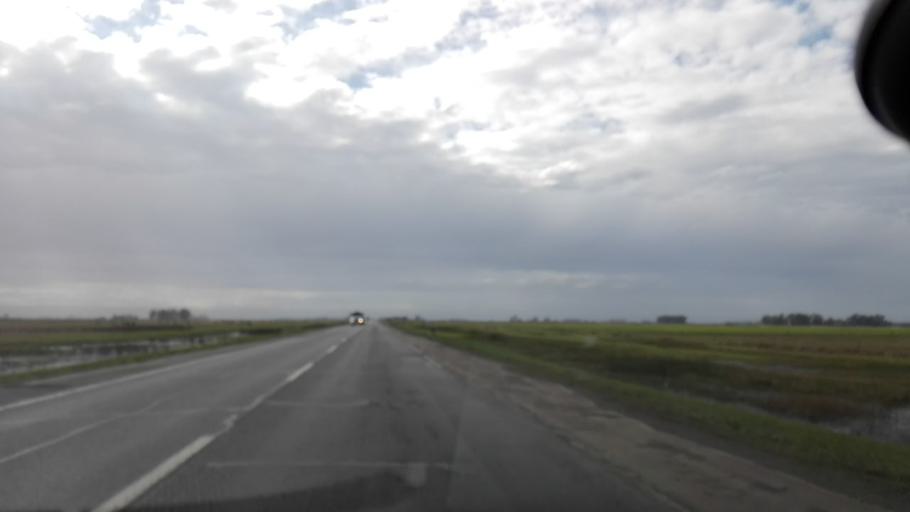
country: AR
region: Buenos Aires
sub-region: Partido de Las Flores
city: Las Flores
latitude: -35.9913
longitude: -59.0543
